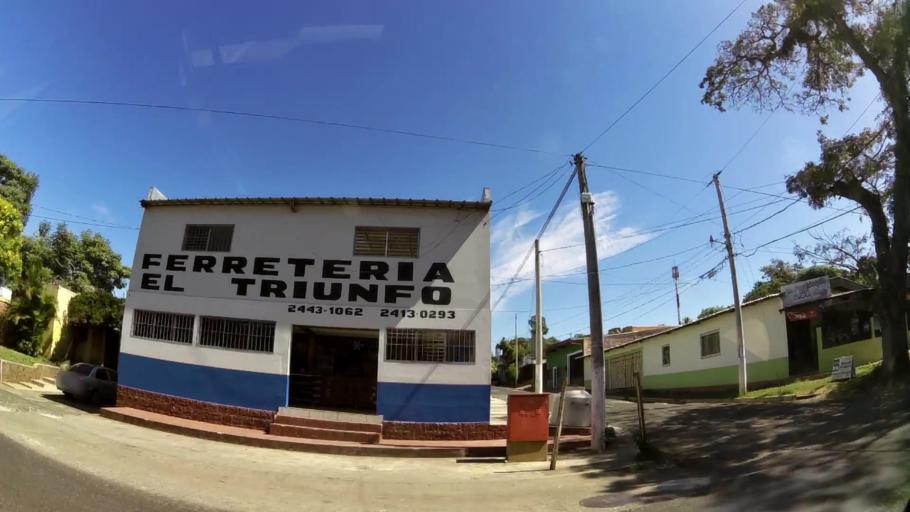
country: SV
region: Ahuachapan
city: Ahuachapan
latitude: 13.9288
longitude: -89.8525
